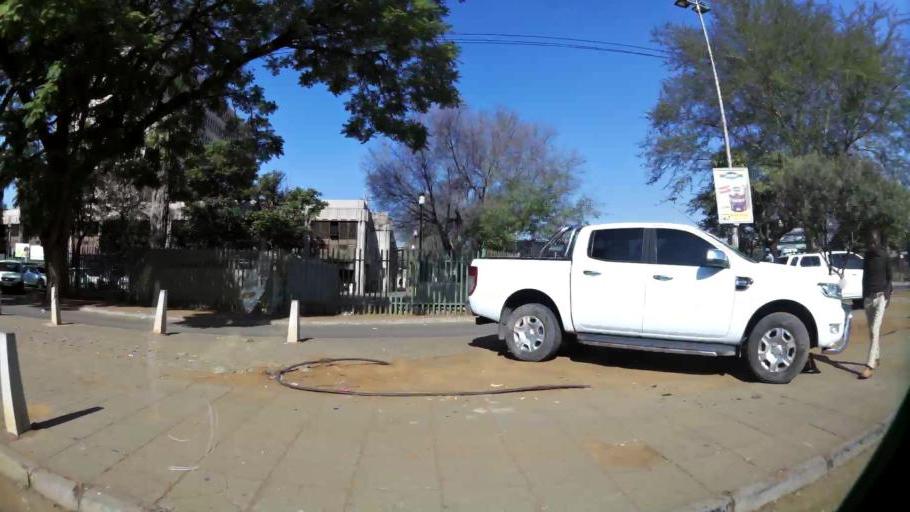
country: ZA
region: North-West
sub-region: Bojanala Platinum District Municipality
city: Rustenburg
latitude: -25.6726
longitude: 27.2434
